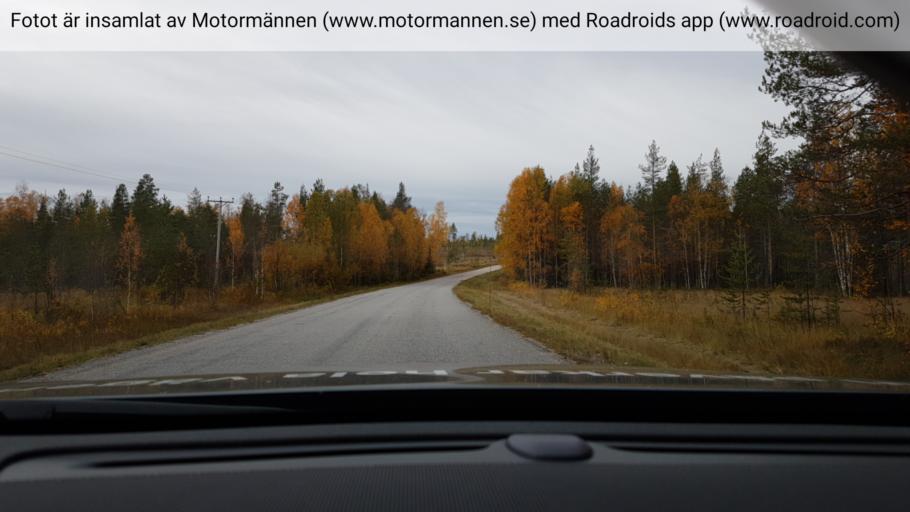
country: SE
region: Norrbotten
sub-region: Overkalix Kommun
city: OEverkalix
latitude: 66.2576
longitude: 23.0731
